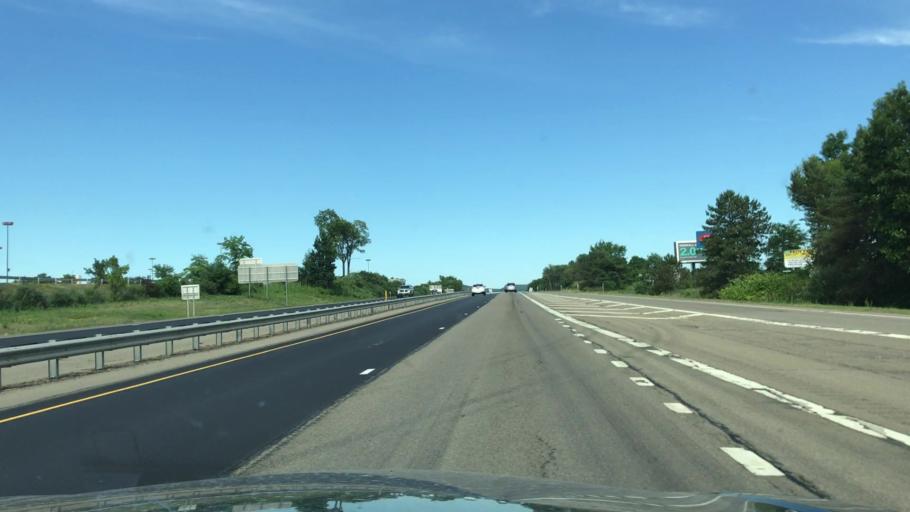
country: US
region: New York
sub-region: Chemung County
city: Horseheads
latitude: 42.1577
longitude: -76.8729
